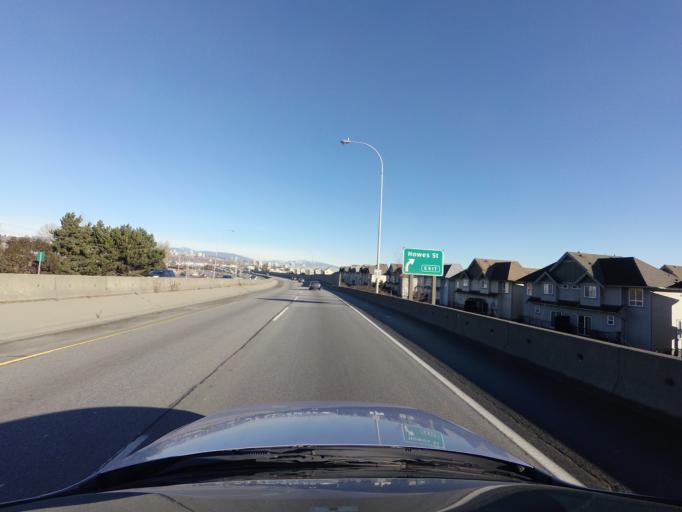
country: CA
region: British Columbia
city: New Westminster
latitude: 49.1840
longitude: -122.9541
